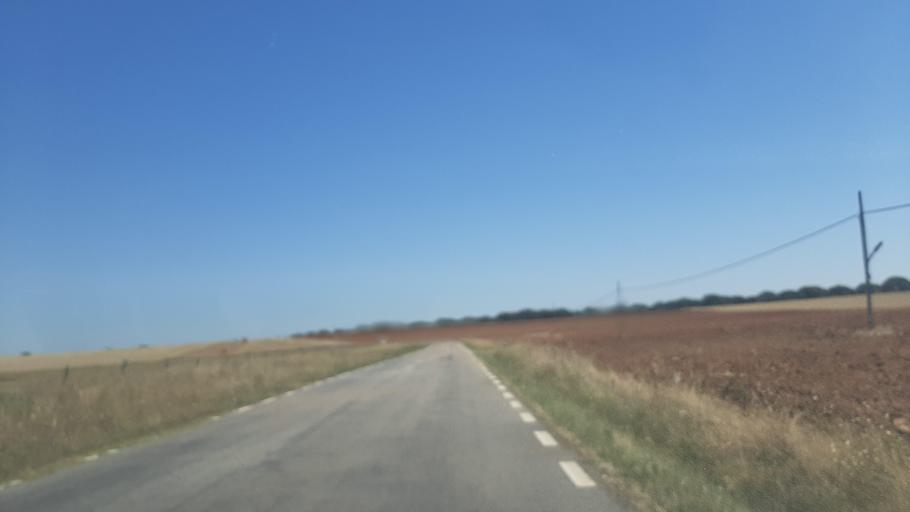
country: ES
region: Castille and Leon
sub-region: Provincia de Salamanca
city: Cabrillas
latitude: 40.7195
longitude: -6.1767
